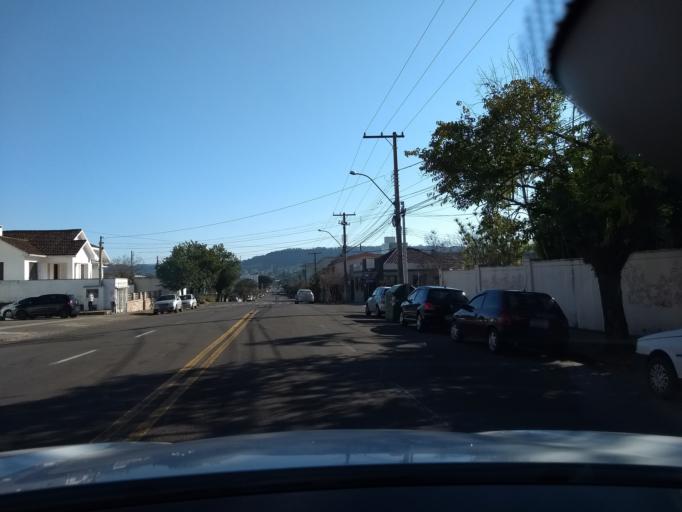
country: BR
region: Rio Grande do Sul
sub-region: Santa Cruz Do Sul
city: Santa Cruz do Sul
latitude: -29.7150
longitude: -52.4357
